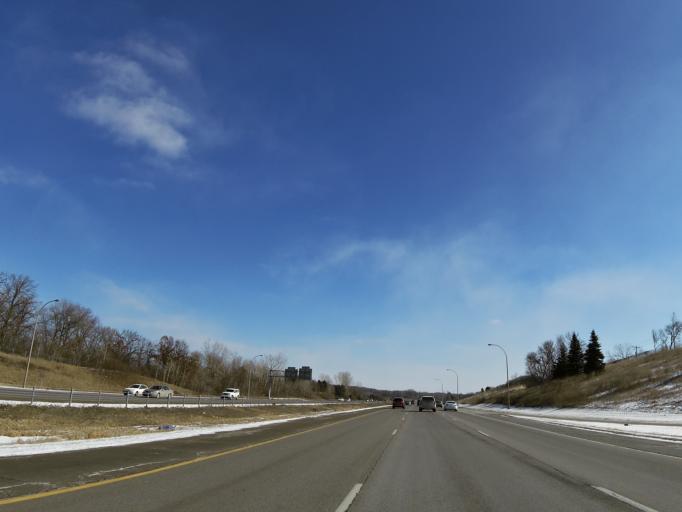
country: US
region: Minnesota
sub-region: Dakota County
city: Mendota Heights
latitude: 44.8621
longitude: -93.1226
